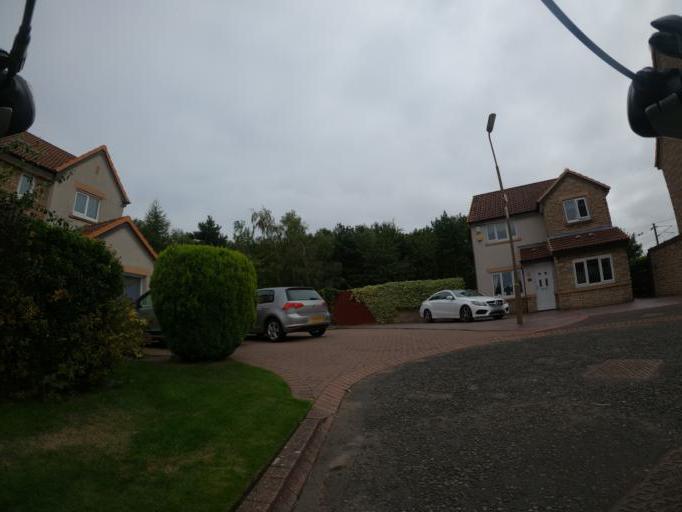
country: GB
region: Scotland
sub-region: East Lothian
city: Musselburgh
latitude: 55.9364
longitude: -3.0947
